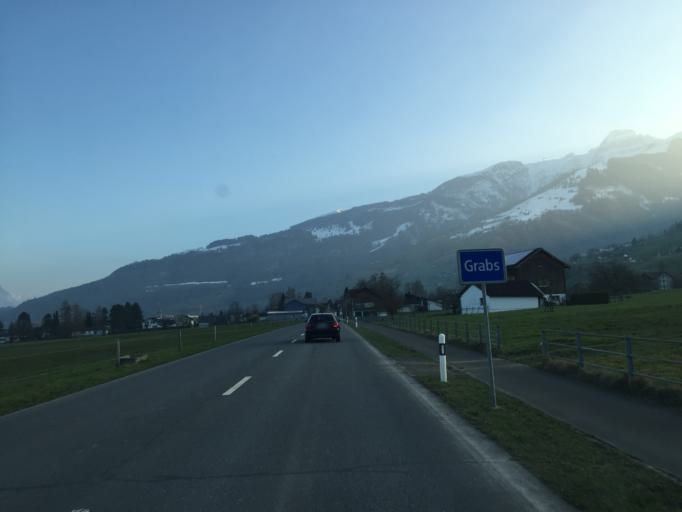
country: CH
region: Saint Gallen
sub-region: Wahlkreis Werdenberg
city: Gams
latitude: 47.1936
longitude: 9.4438
